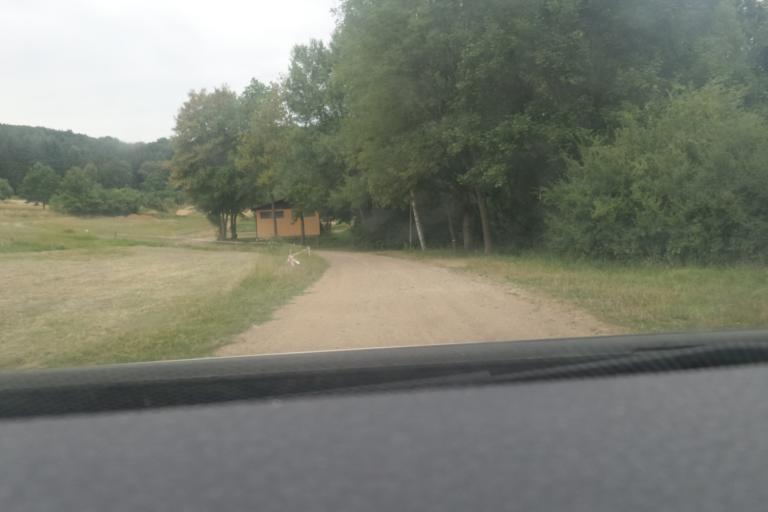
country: DE
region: Hesse
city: Beuern
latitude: 50.6298
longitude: 8.8125
